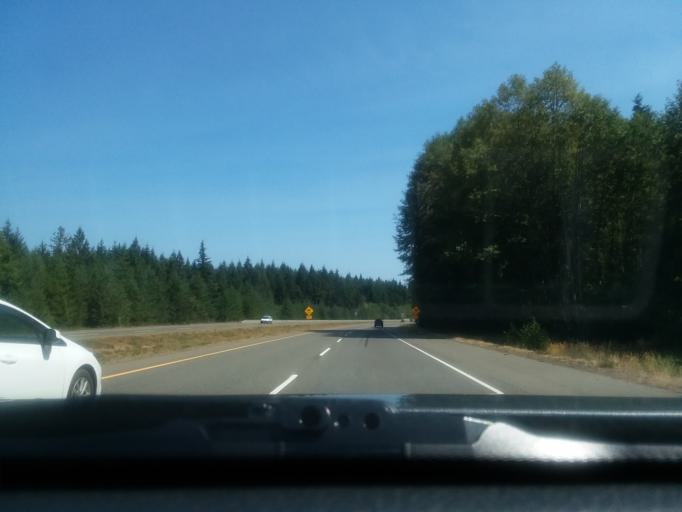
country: CA
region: British Columbia
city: Port Alberni
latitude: 49.4200
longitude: -124.7095
